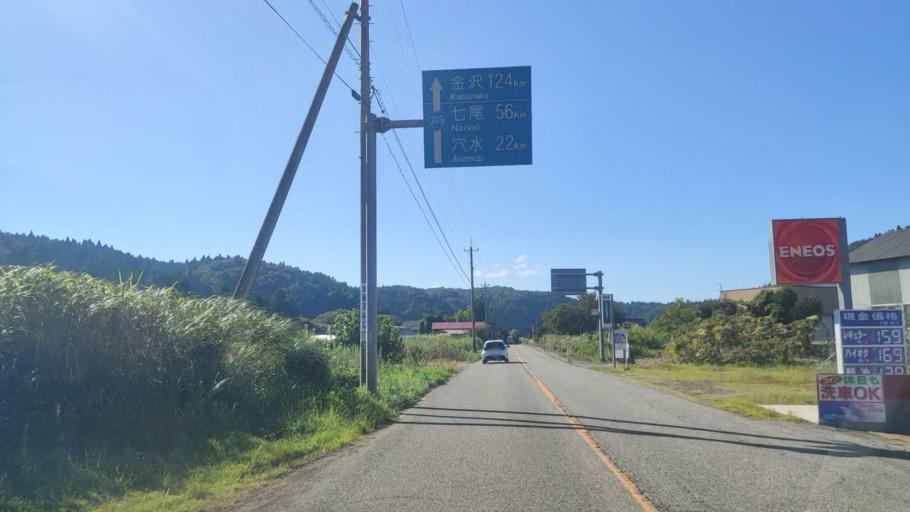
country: JP
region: Ishikawa
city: Nanao
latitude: 37.2560
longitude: 137.0810
